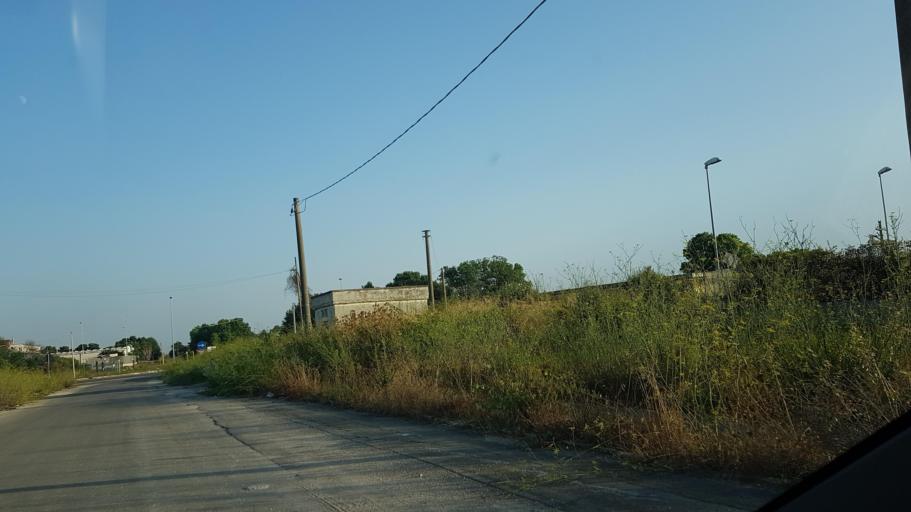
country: IT
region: Apulia
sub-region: Provincia di Brindisi
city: Materdomini
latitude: 40.6364
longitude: 17.9720
